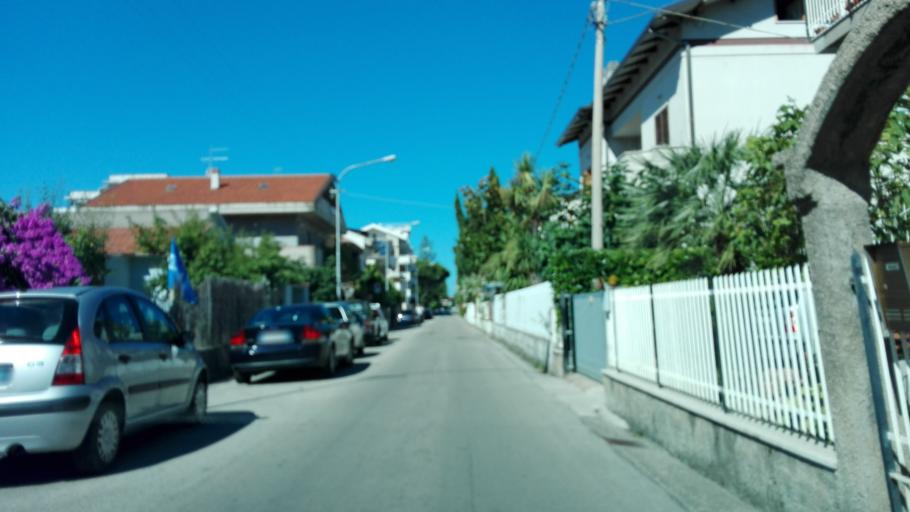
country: IT
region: Abruzzo
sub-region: Provincia di Pescara
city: Montesilvano Marina
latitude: 42.5091
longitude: 14.1559
